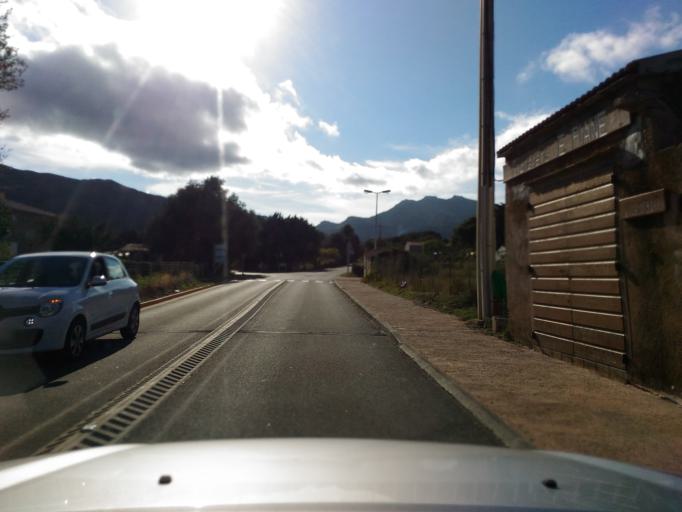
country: FR
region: Corsica
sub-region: Departement de la Haute-Corse
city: Brando
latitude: 42.9568
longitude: 9.4463
